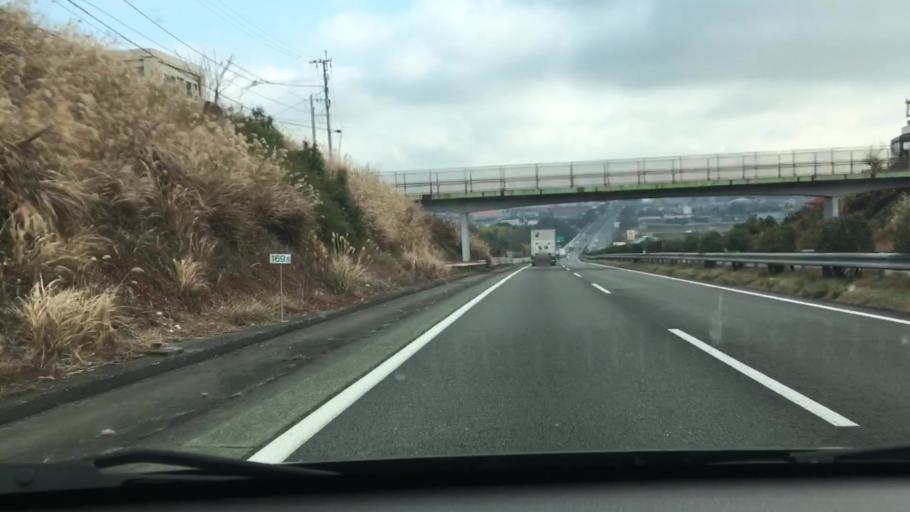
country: JP
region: Kumamoto
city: Kumamoto
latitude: 32.8475
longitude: 130.7688
